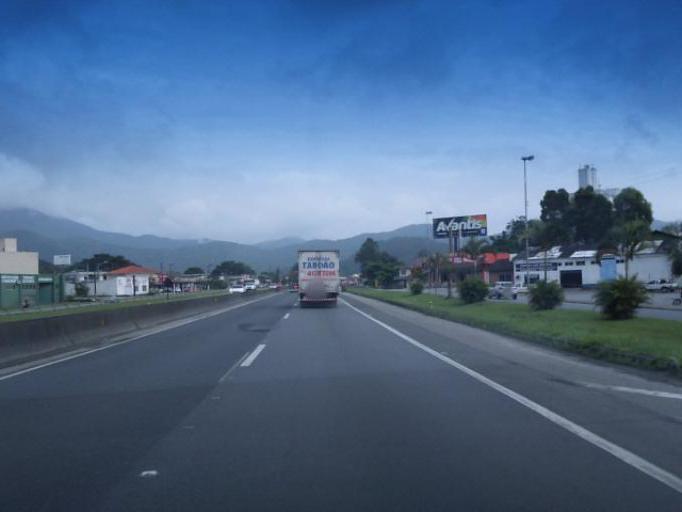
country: BR
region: Santa Catarina
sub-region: Itapema
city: Itapema
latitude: -27.1044
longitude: -48.6161
